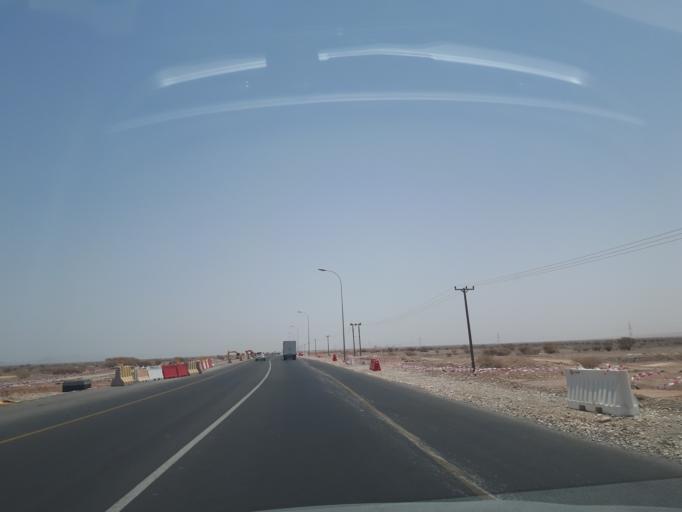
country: OM
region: Ash Sharqiyah
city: Badiyah
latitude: 22.4284
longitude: 59.0368
